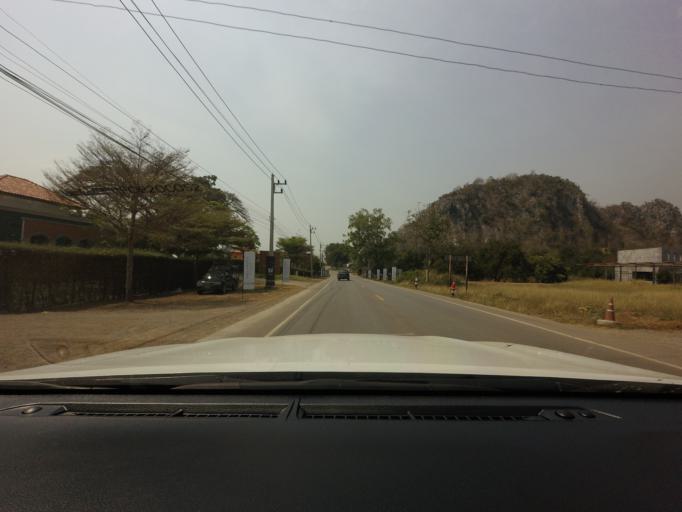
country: TH
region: Sara Buri
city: Muak Lek
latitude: 14.5861
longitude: 101.2467
